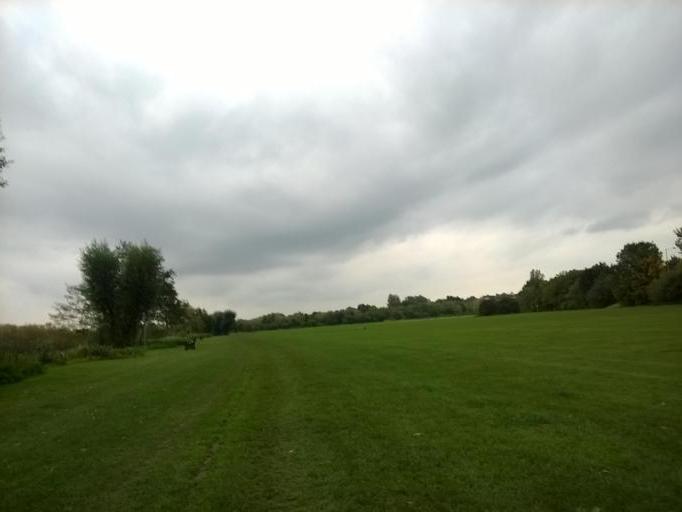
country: GB
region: England
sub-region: Wokingham
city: Earley
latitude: 51.4613
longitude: -0.9399
